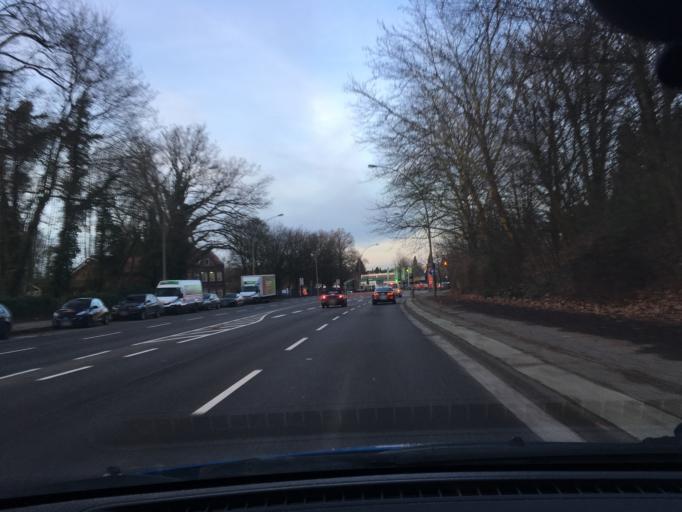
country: DE
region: Lower Saxony
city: Seevetal
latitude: 53.4230
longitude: 9.9809
